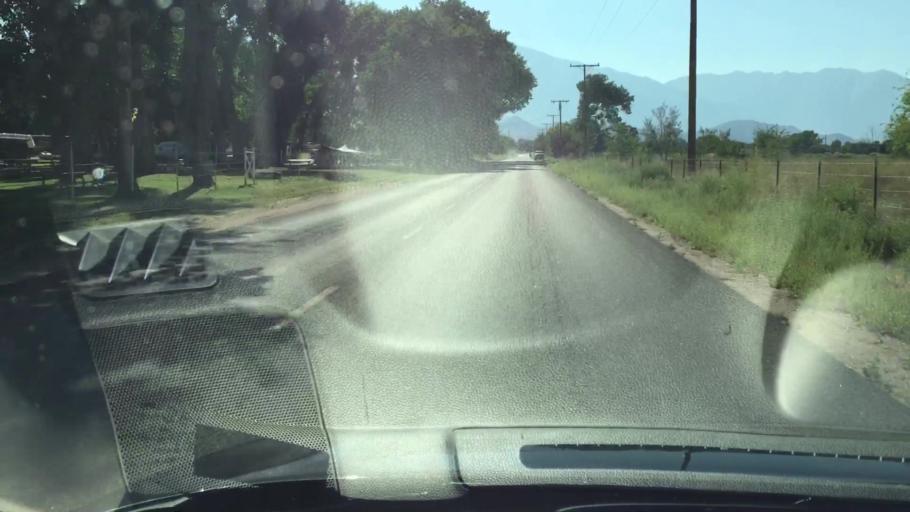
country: US
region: California
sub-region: Inyo County
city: Bishop
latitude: 37.3468
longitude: -118.3978
